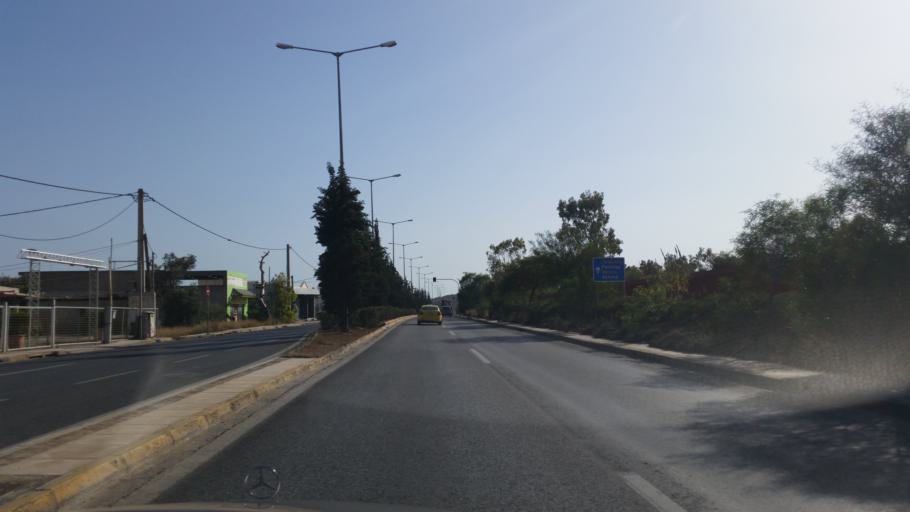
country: GR
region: Attica
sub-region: Nomarchia Anatolikis Attikis
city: Vari
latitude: 37.8429
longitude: 23.8182
